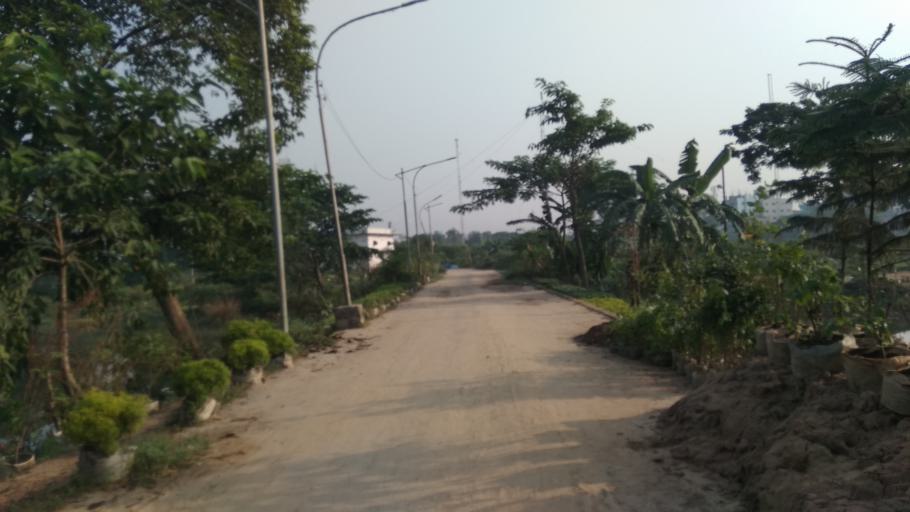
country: BD
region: Dhaka
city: Tungi
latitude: 23.8411
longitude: 90.4193
